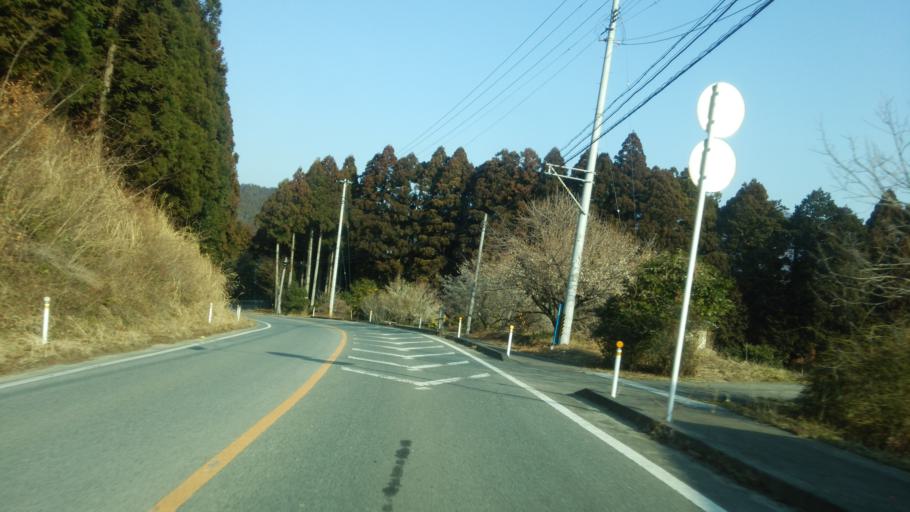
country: JP
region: Fukushima
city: Iwaki
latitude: 37.0639
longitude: 140.8067
